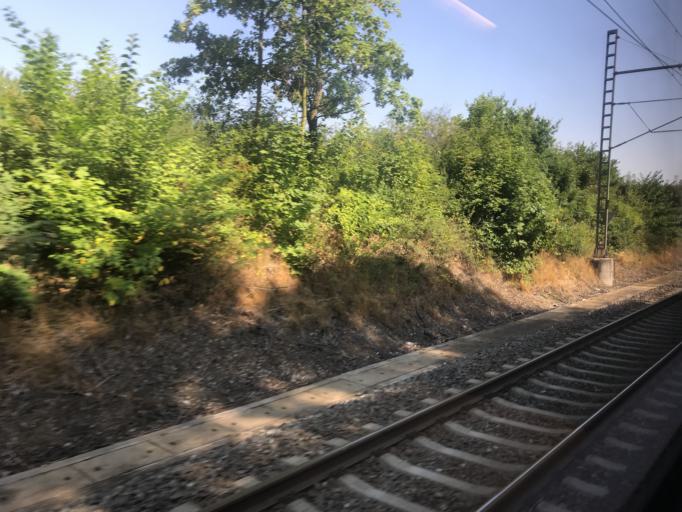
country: CZ
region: Central Bohemia
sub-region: Okres Praha-Vychod
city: Ricany
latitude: 49.9760
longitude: 14.6652
